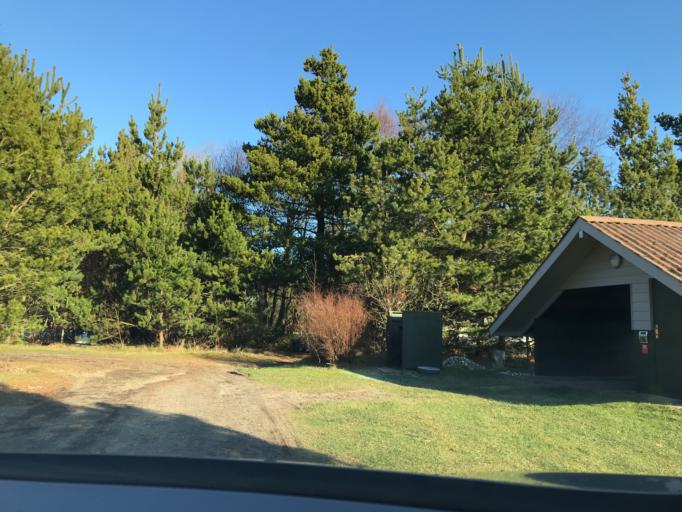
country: DK
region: South Denmark
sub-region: Varde Kommune
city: Oksbol
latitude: 55.7757
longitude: 8.2453
